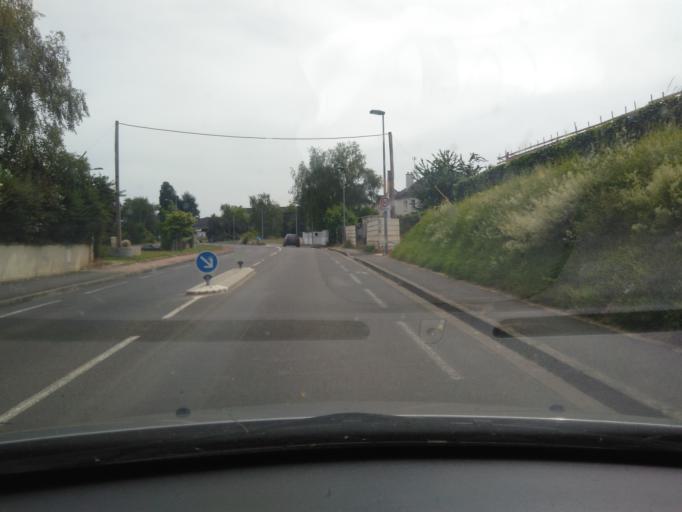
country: FR
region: Centre
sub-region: Departement d'Indre-et-Loire
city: Amboise
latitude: 47.4032
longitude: 1.0100
